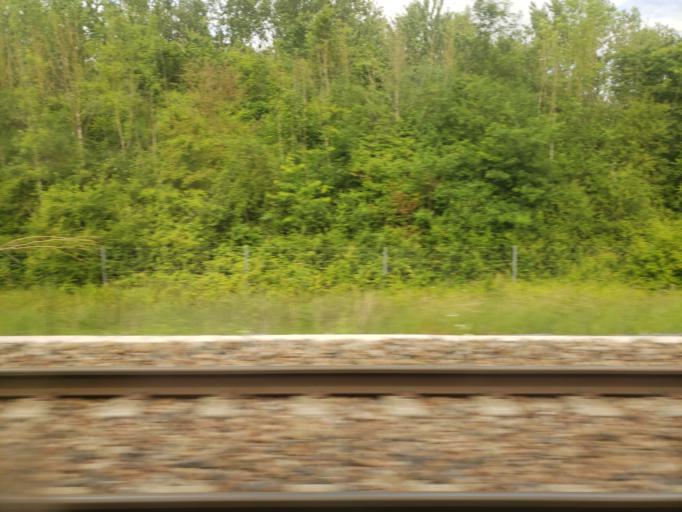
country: FR
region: Ile-de-France
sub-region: Departement de Seine-et-Marne
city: Serris
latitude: 48.8169
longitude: 2.7847
